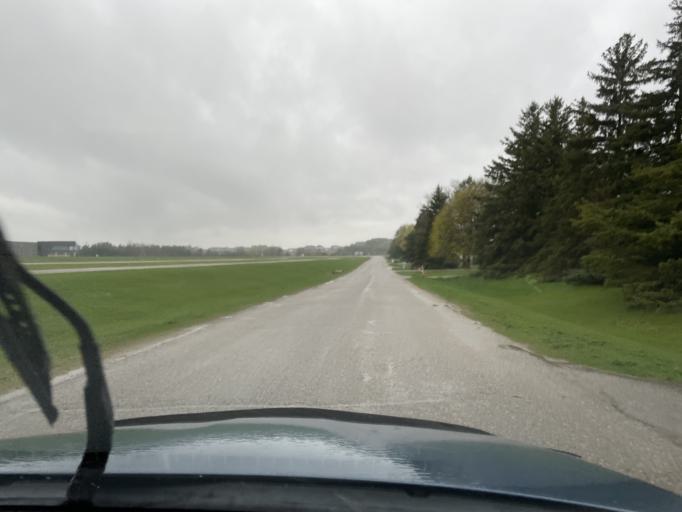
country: CA
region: Ontario
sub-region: Wellington County
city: Guelph
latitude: 43.5657
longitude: -80.1985
